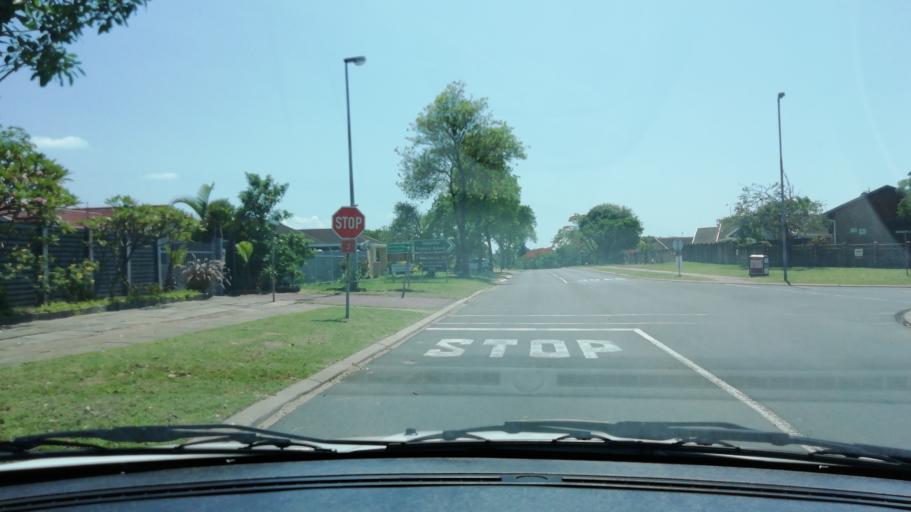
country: ZA
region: KwaZulu-Natal
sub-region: uThungulu District Municipality
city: Richards Bay
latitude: -28.7372
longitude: 32.0554
